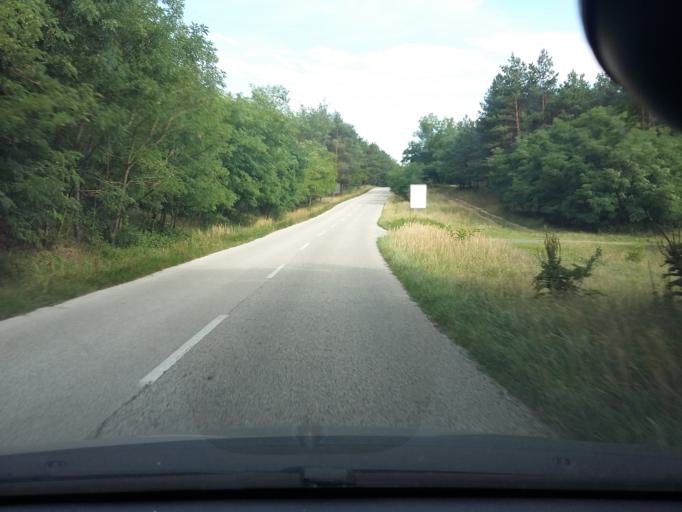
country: SK
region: Trnavsky
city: Gbely
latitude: 48.5671
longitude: 17.2176
